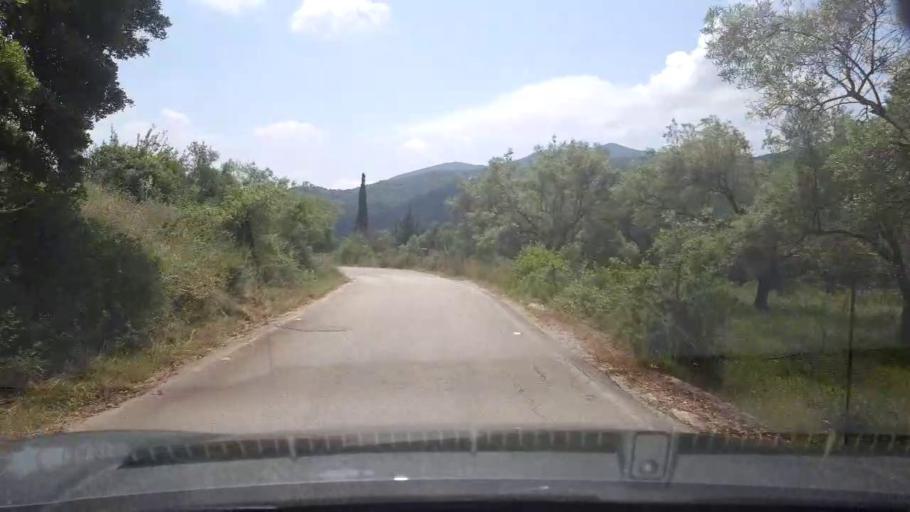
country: GR
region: Ionian Islands
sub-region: Lefkada
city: Nidri
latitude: 38.6450
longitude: 20.6996
